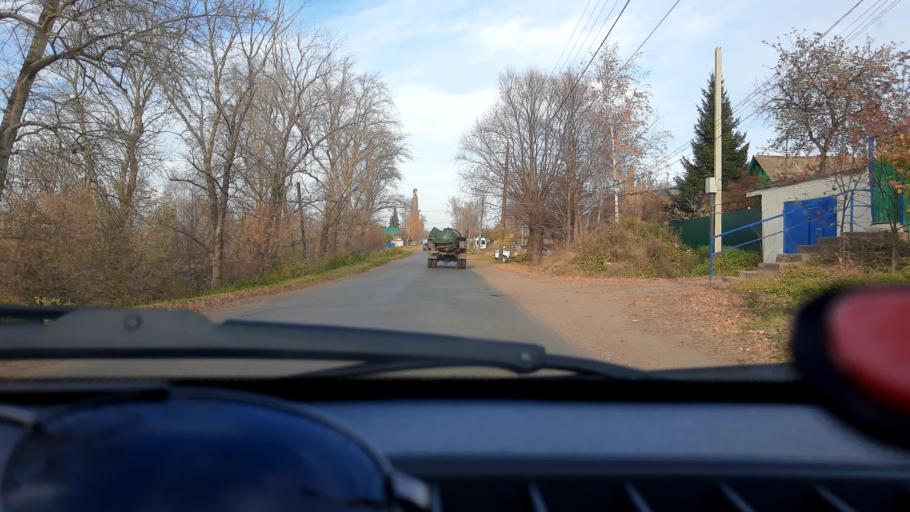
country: RU
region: Bashkortostan
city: Ufa
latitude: 54.8353
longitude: 56.1432
